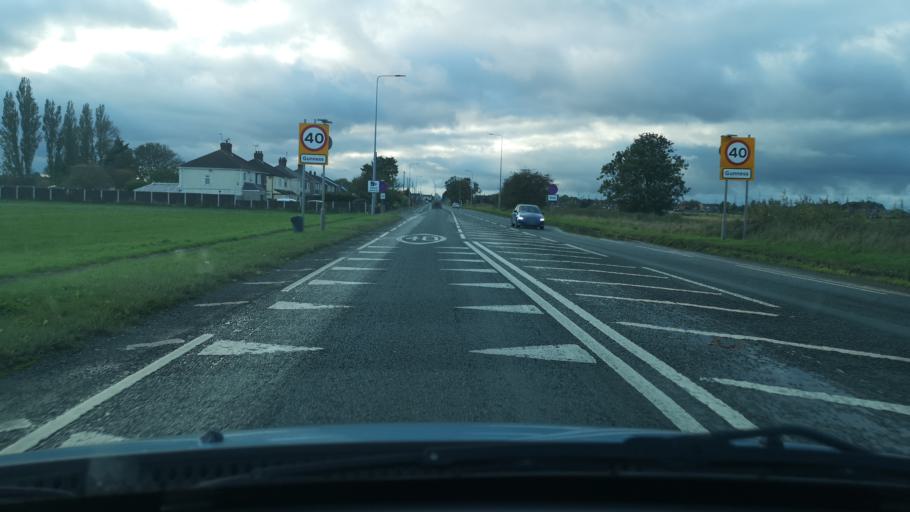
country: GB
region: England
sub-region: North Lincolnshire
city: Gunness
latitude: 53.5901
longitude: -0.7182
